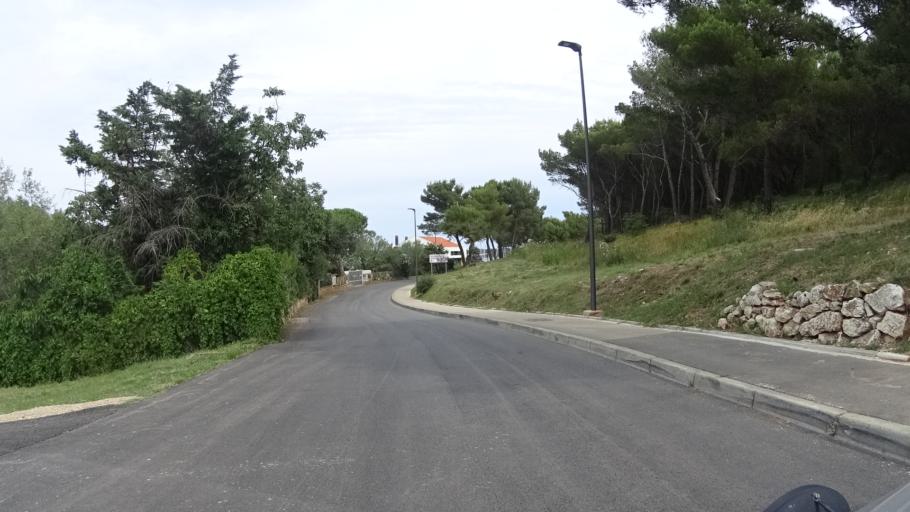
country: HR
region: Istarska
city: Medulin
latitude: 44.8230
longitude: 13.8989
